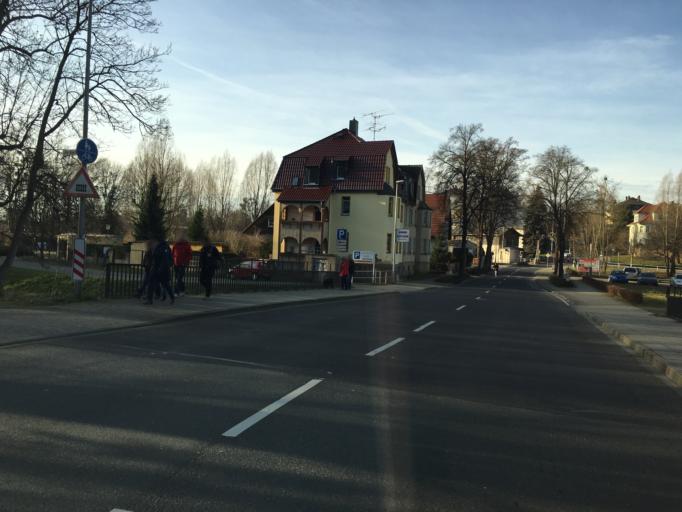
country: DE
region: Saxony
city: Oschatz
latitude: 51.2945
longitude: 13.1126
